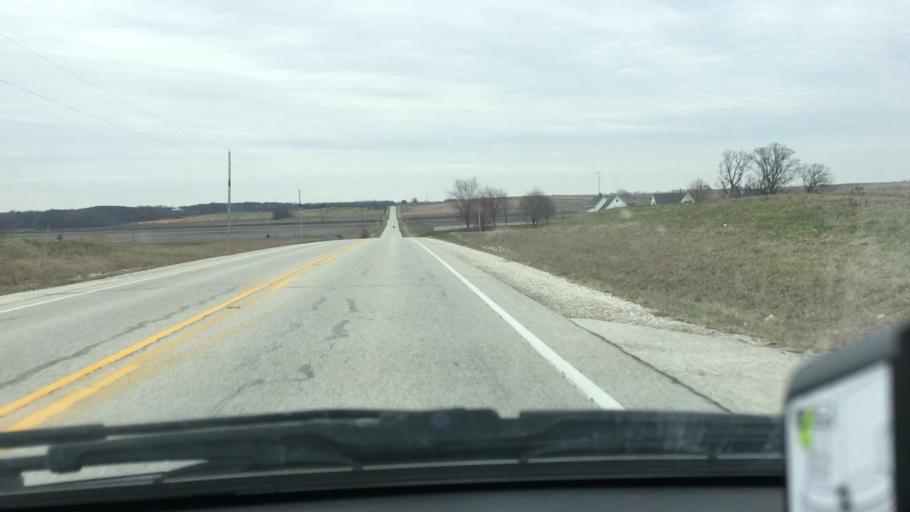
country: US
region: Indiana
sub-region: Greene County
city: Bloomfield
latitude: 38.9968
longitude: -87.0163
